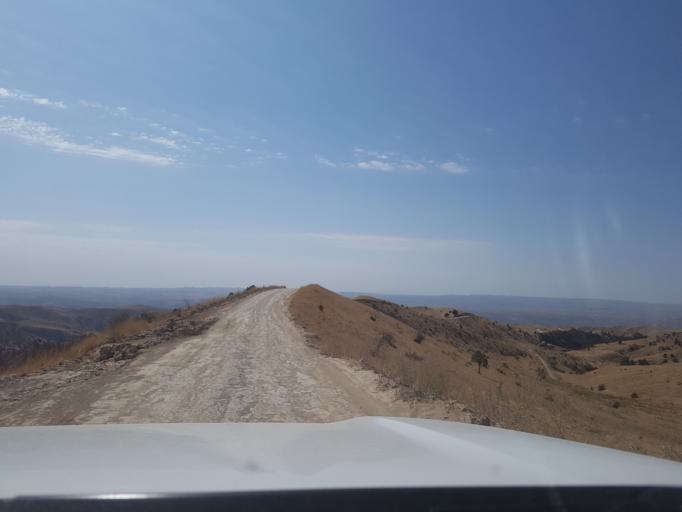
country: TM
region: Ahal
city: Baharly
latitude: 38.2916
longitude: 56.9337
